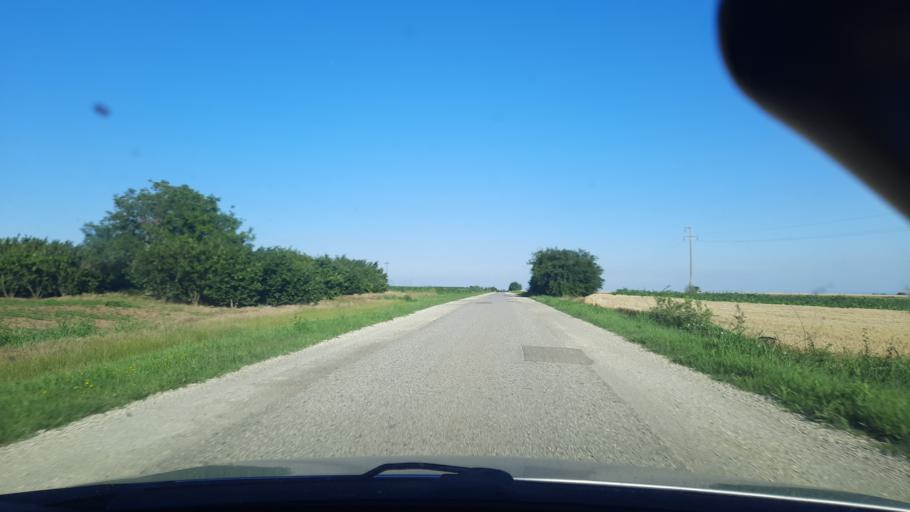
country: RS
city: Cortanovci
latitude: 45.1116
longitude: 19.9699
